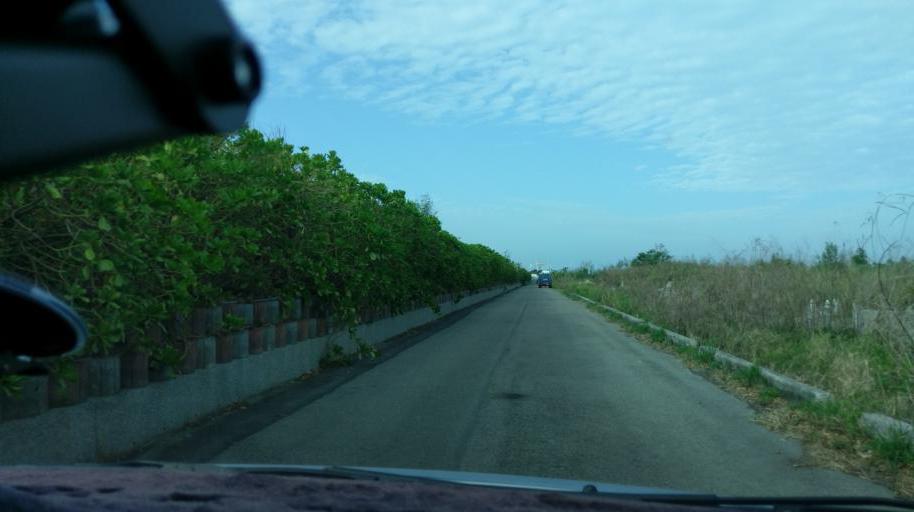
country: TW
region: Taiwan
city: Fengyuan
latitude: 24.3180
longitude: 120.5515
